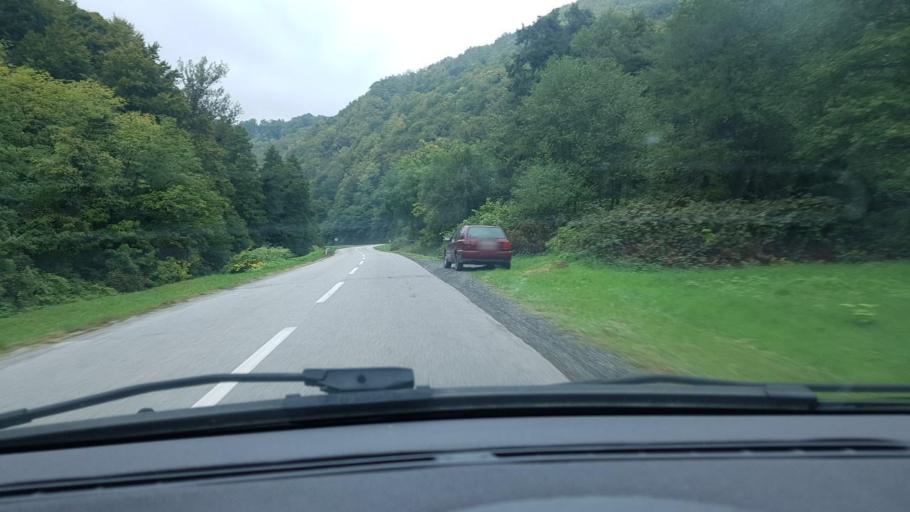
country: HR
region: Krapinsko-Zagorska
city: Marija Bistrica
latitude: 45.9359
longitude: 16.1127
